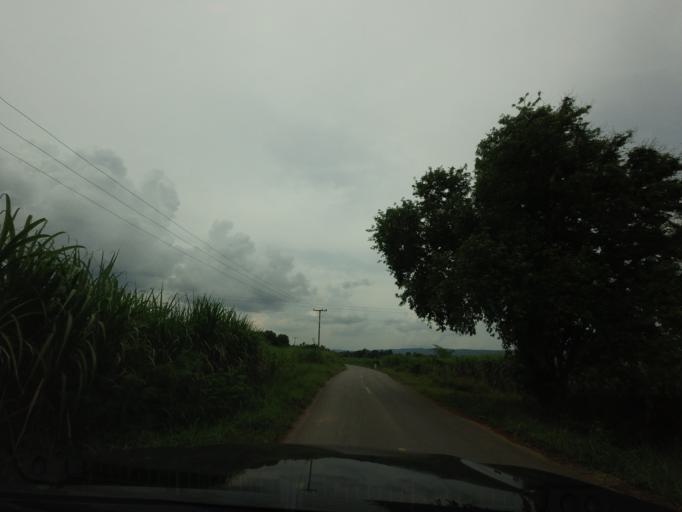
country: TH
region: Changwat Nong Bua Lamphu
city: Nong Bua Lamphu
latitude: 17.2601
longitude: 102.3875
